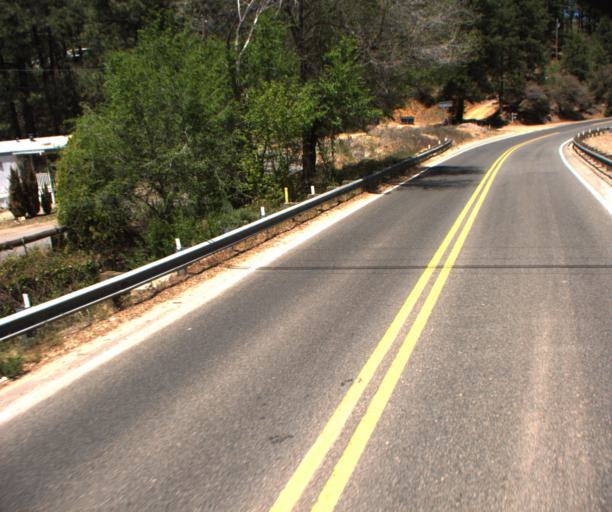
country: US
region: Arizona
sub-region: Yavapai County
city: Prescott
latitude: 34.5134
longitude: -112.4775
